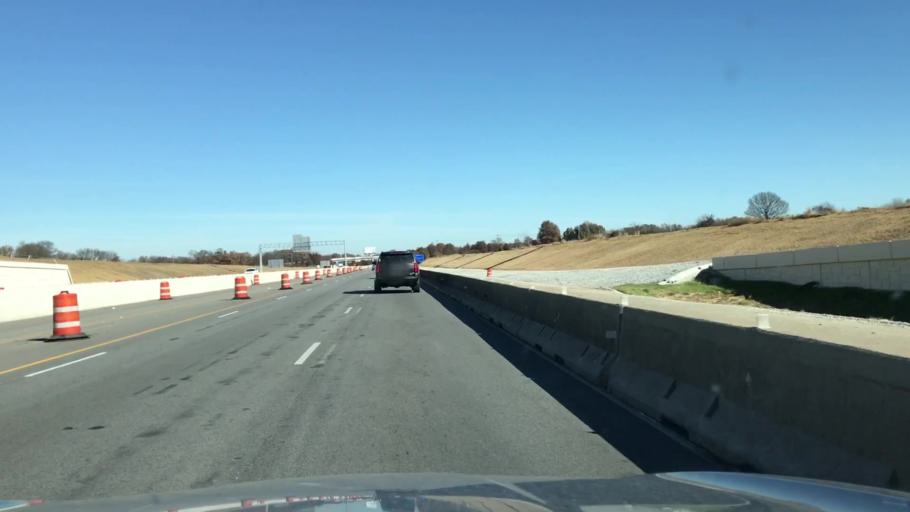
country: US
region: Arkansas
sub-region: Benton County
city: Bentonville
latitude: 36.3658
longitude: -94.1739
